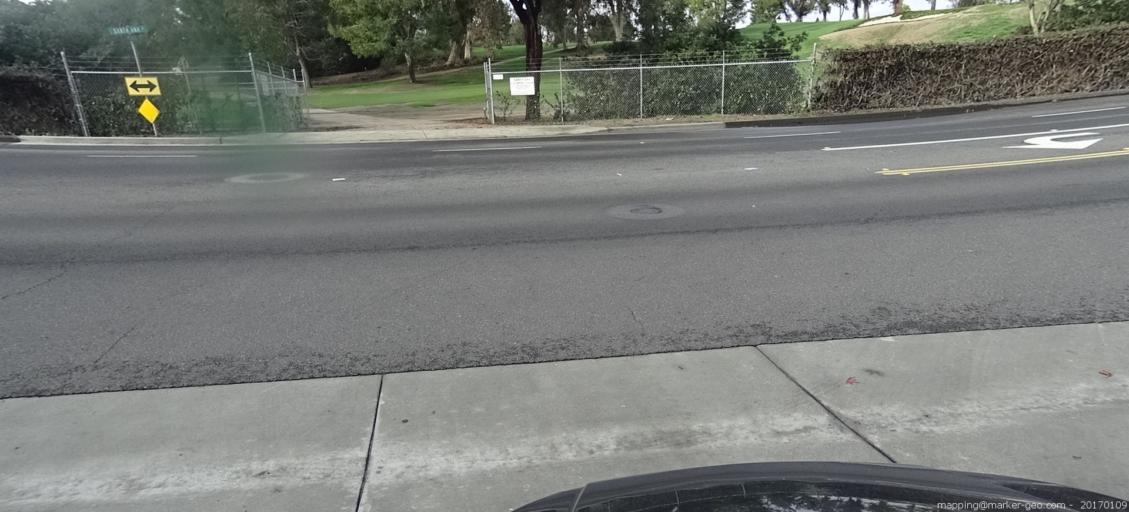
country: US
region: California
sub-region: Orange County
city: Costa Mesa
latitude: 33.6643
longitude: -117.8842
